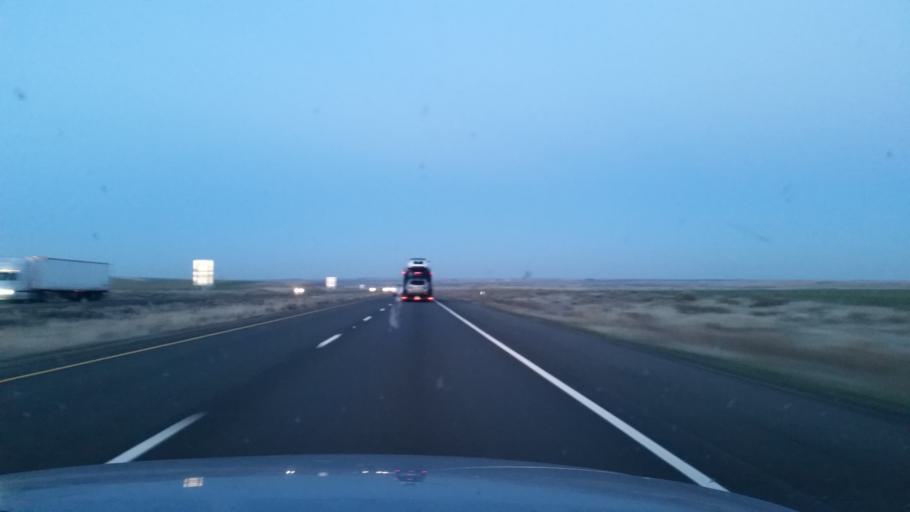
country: US
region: Washington
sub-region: Adams County
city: Ritzville
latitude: 47.1304
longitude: -118.3456
